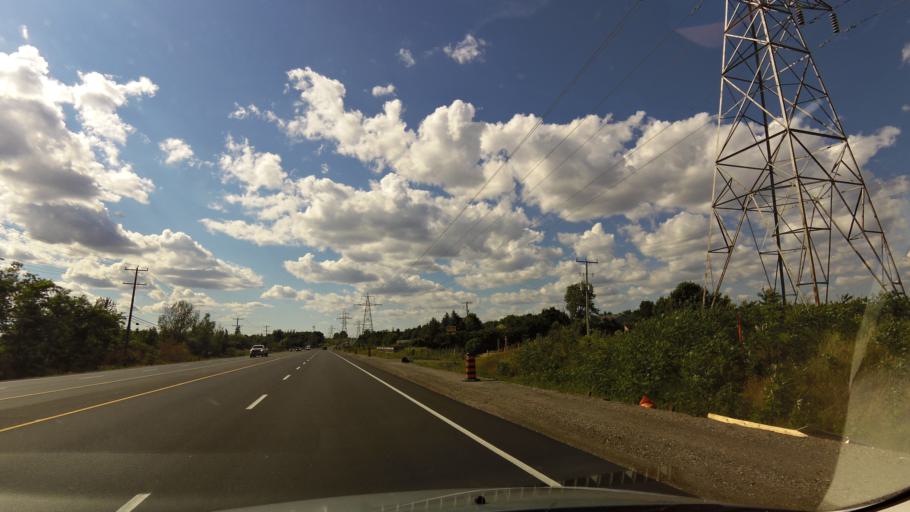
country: CA
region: Ontario
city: Ancaster
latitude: 43.3920
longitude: -80.0261
